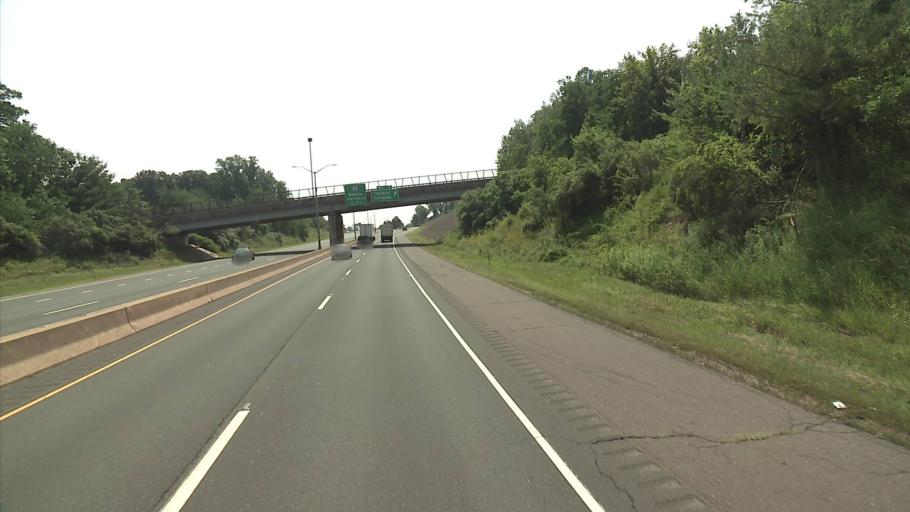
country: US
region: Connecticut
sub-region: Hartford County
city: East Hartford
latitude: 41.7976
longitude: -72.5778
